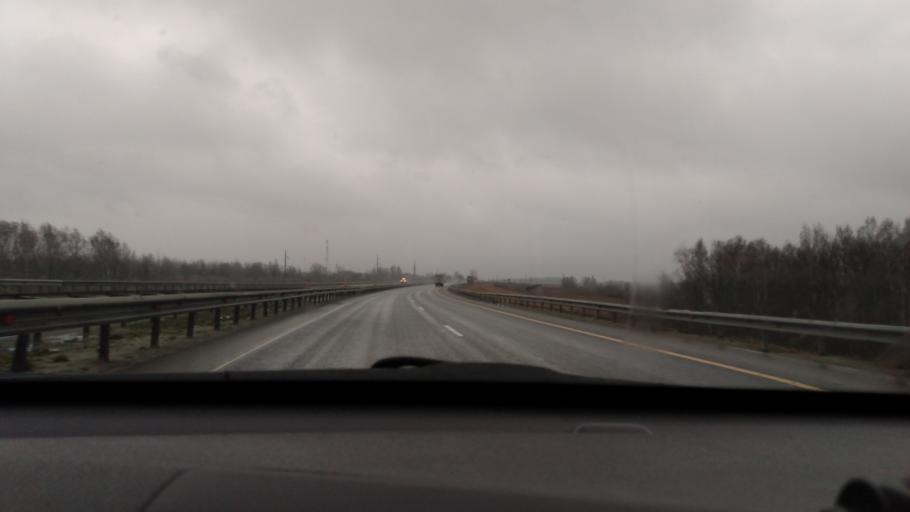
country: RU
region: Moskovskaya
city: Kashira
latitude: 54.7785
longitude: 38.1296
